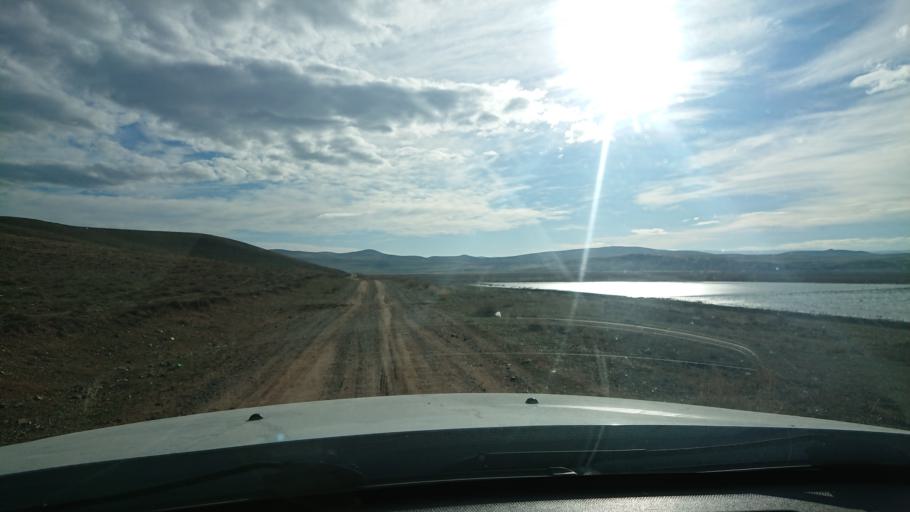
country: TR
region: Aksaray
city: Sariyahsi
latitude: 39.0450
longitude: 33.9714
